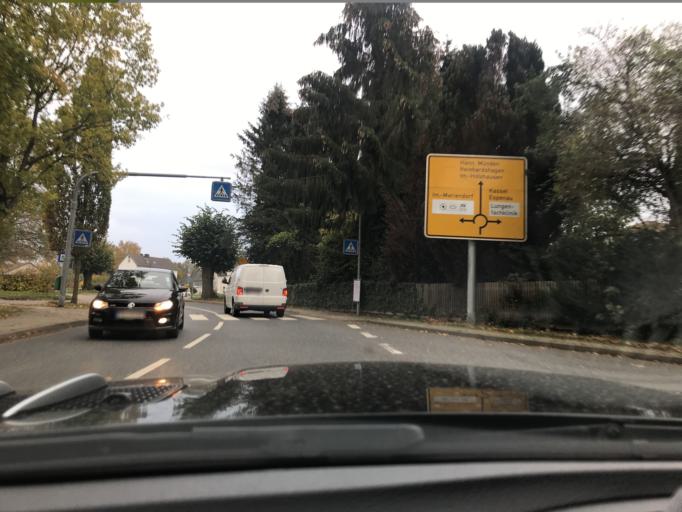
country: DE
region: Hesse
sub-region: Regierungsbezirk Kassel
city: Immenhausen
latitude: 51.4260
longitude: 9.4780
